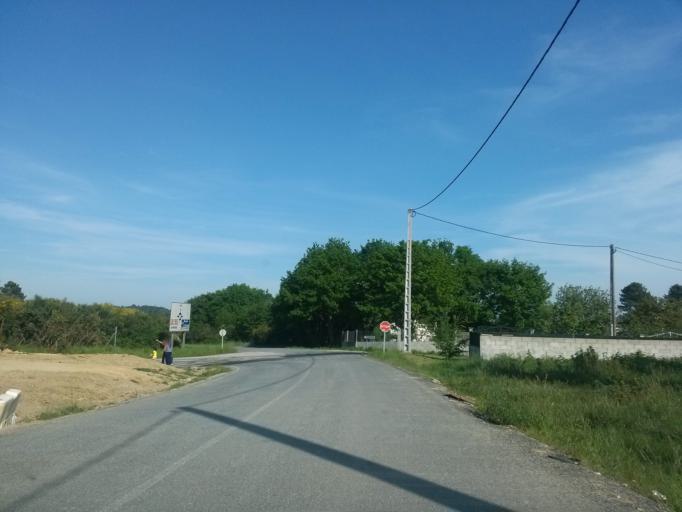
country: ES
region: Galicia
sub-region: Provincia de Lugo
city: Lugo
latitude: 43.0333
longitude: -7.5488
